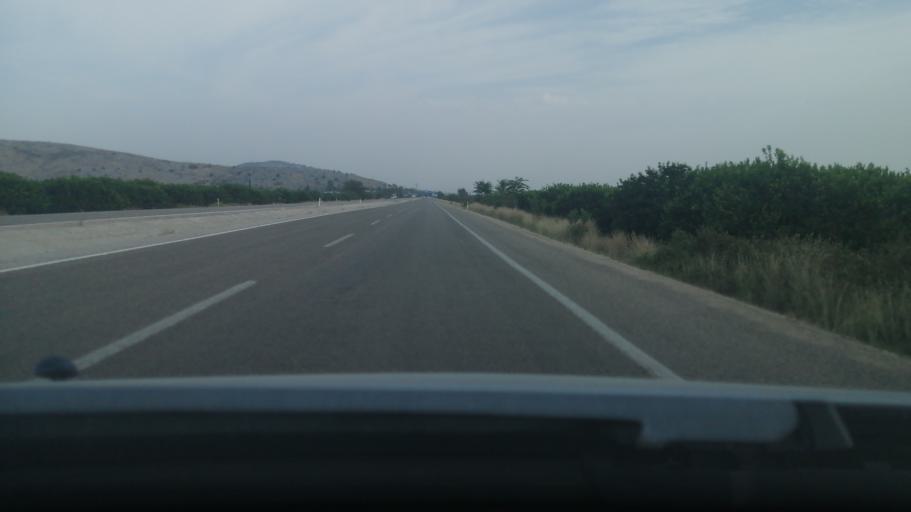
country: TR
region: Adana
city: Kozan
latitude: 37.3836
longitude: 35.8128
